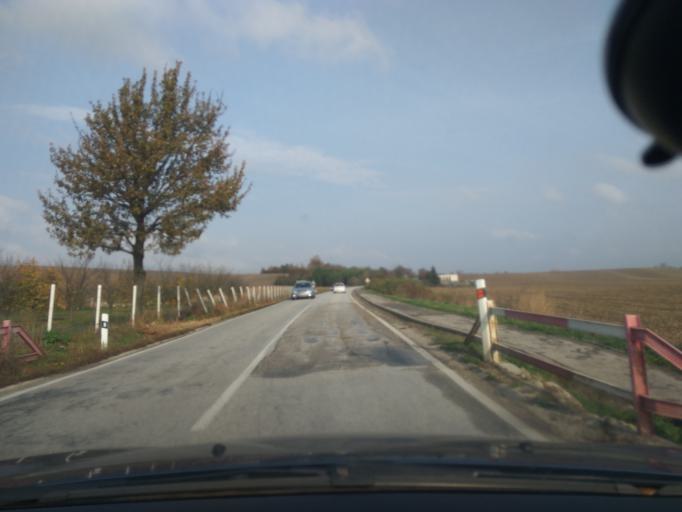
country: SK
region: Trnavsky
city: Vrbove
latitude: 48.6564
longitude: 17.7567
